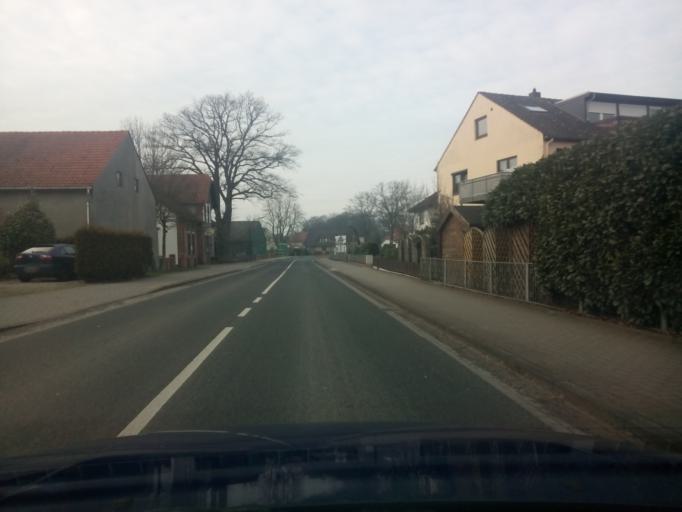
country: DE
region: Lower Saxony
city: Oyten
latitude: 53.0772
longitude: 9.0180
